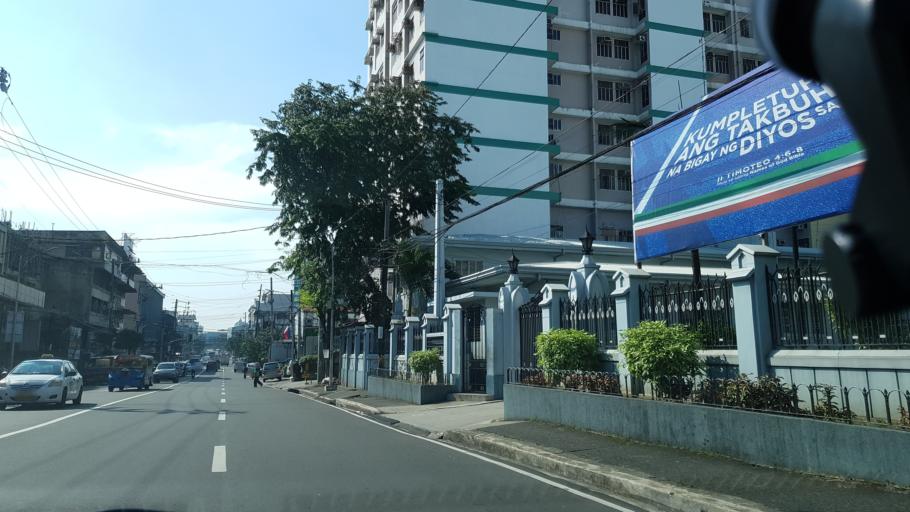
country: PH
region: Metro Manila
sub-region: San Juan
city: San Juan
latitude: 14.6224
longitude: 121.0466
